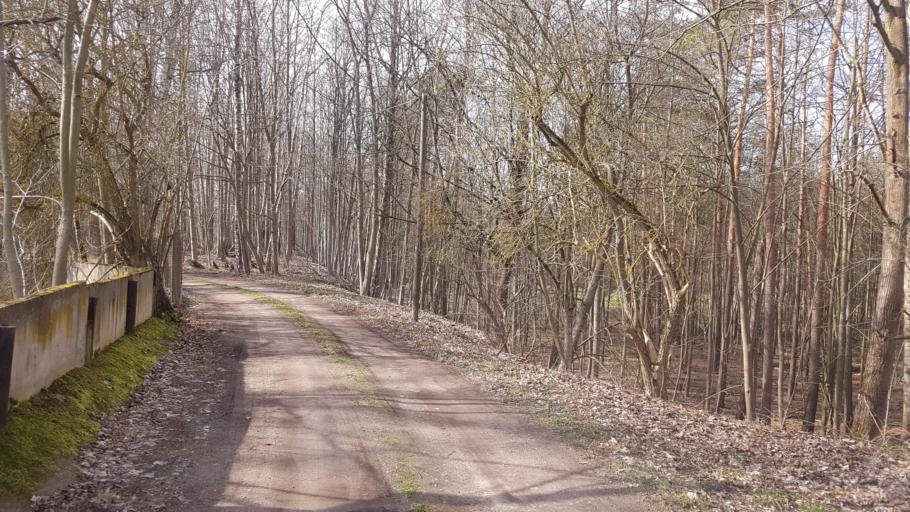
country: DE
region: Brandenburg
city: Schonewalde
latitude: 51.6264
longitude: 13.6179
